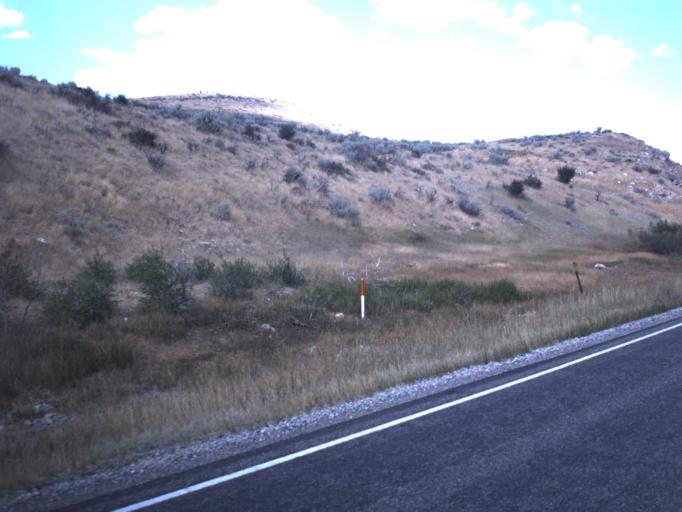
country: US
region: Utah
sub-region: Rich County
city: Randolph
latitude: 41.8636
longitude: -111.3648
